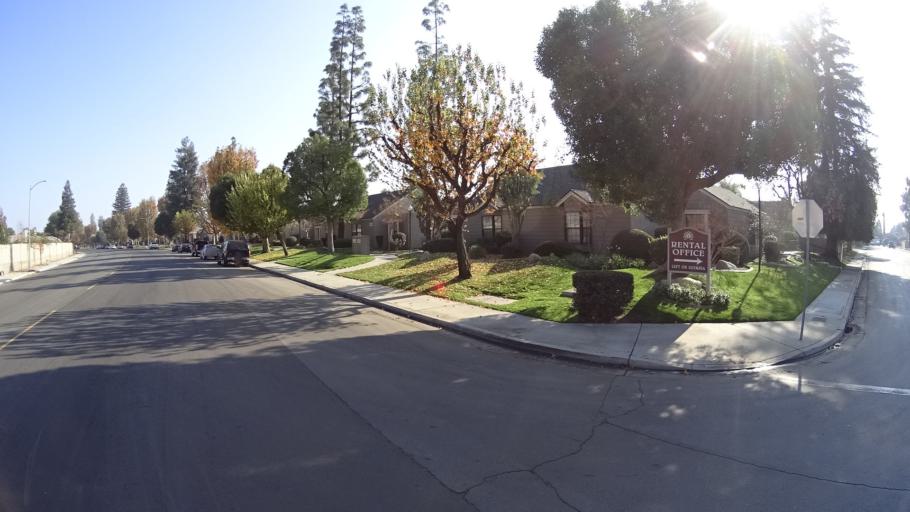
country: US
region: California
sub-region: Kern County
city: Greenacres
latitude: 35.3220
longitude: -119.0789
